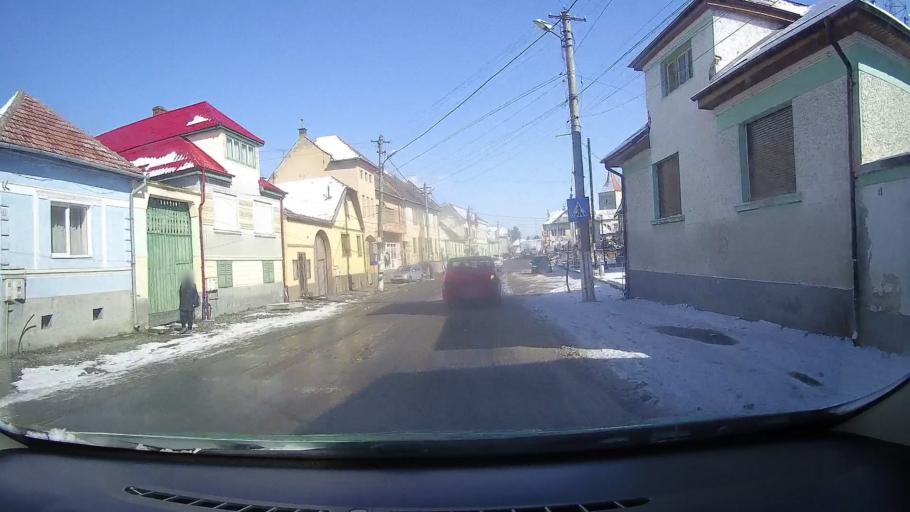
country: RO
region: Sibiu
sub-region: Comuna Avrig
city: Avrig
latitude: 45.7266
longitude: 24.3752
